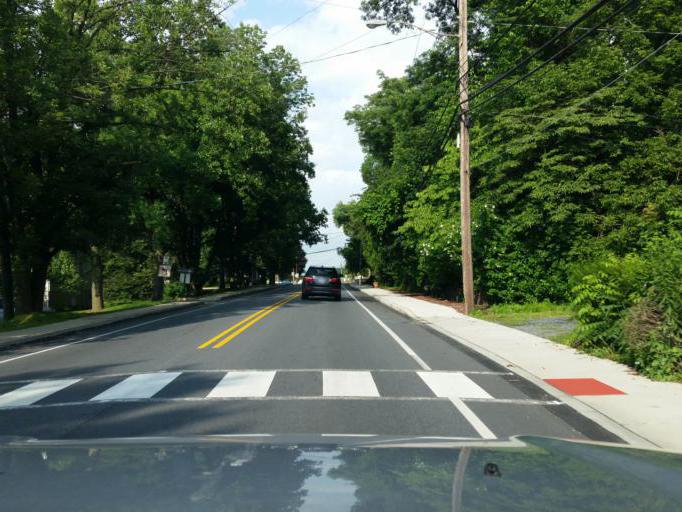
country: US
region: Pennsylvania
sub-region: Dauphin County
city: Hummelstown
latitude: 40.2668
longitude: -76.6956
